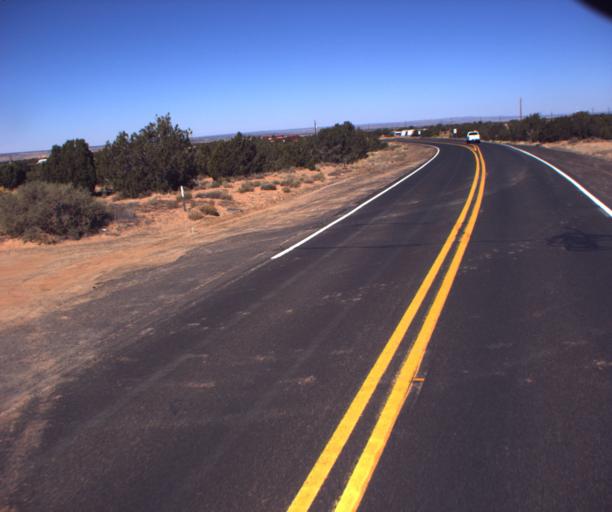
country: US
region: Arizona
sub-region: Navajo County
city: First Mesa
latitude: 35.8381
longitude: -110.5267
